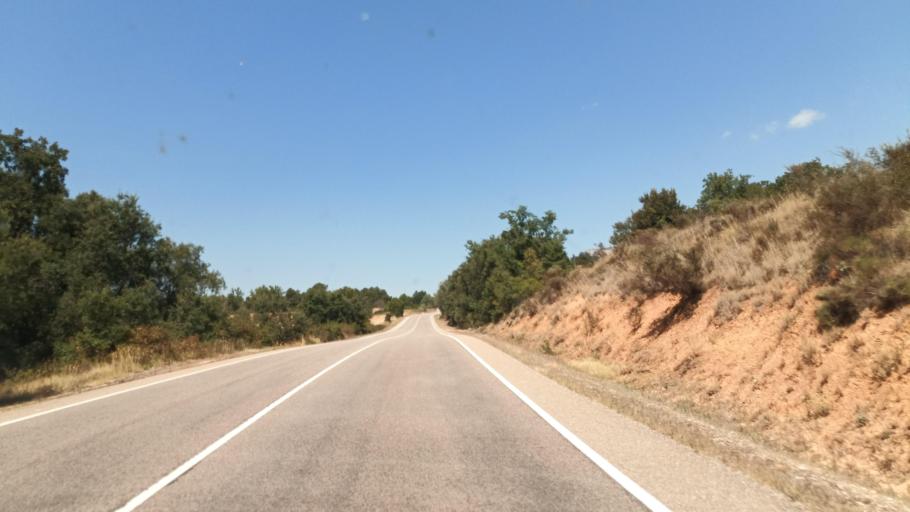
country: ES
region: Castille and Leon
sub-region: Provincia de Burgos
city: Llano de Bureba
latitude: 42.6590
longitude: -3.4028
